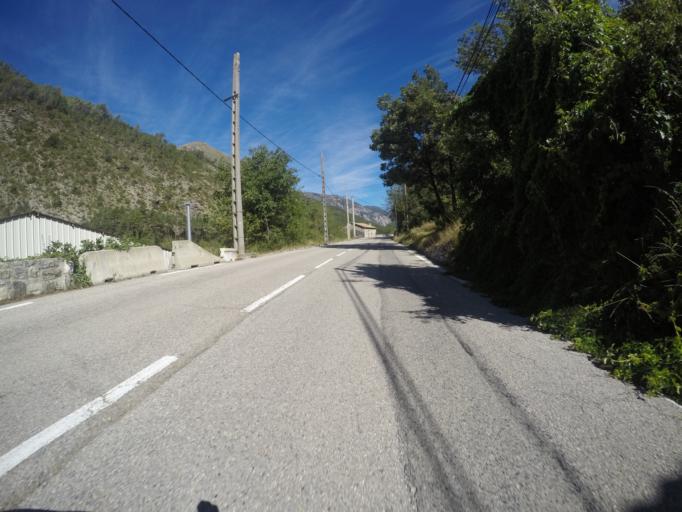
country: FR
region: Provence-Alpes-Cote d'Azur
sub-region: Departement des Alpes-Maritimes
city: Gilette
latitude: 43.9471
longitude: 7.1607
